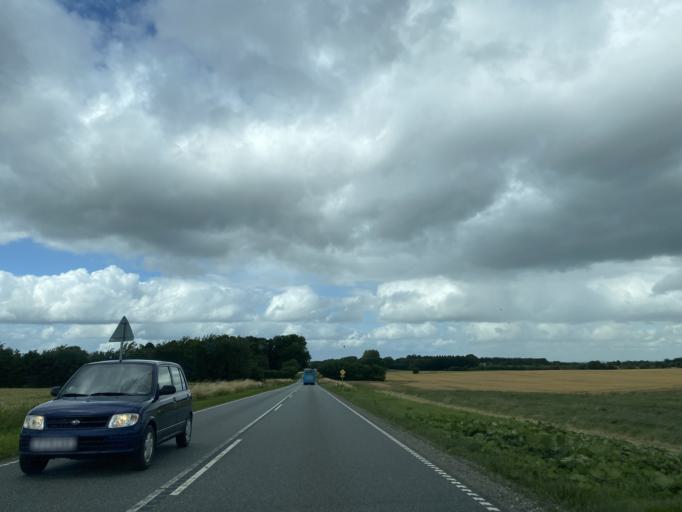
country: DK
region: Central Jutland
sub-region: Silkeborg Kommune
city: Silkeborg
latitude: 56.2402
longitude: 9.6237
